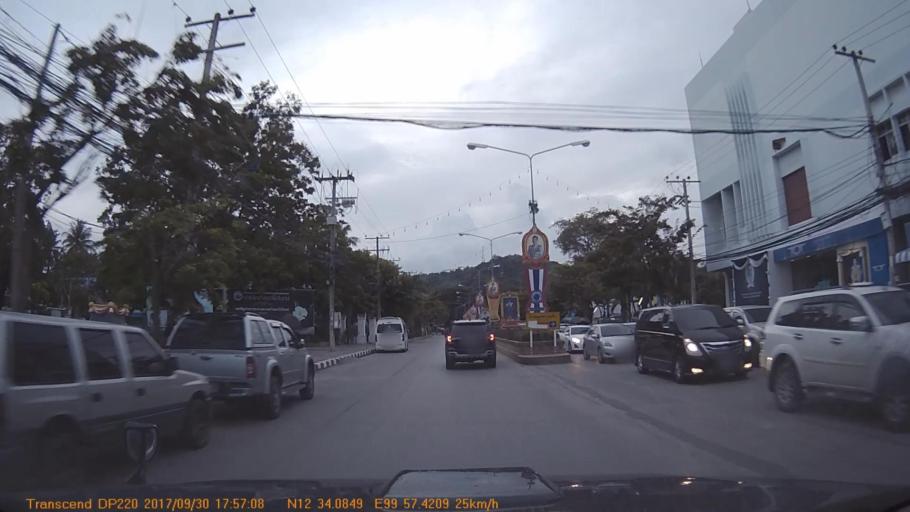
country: TH
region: Prachuap Khiri Khan
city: Hua Hin
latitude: 12.5682
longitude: 99.9570
